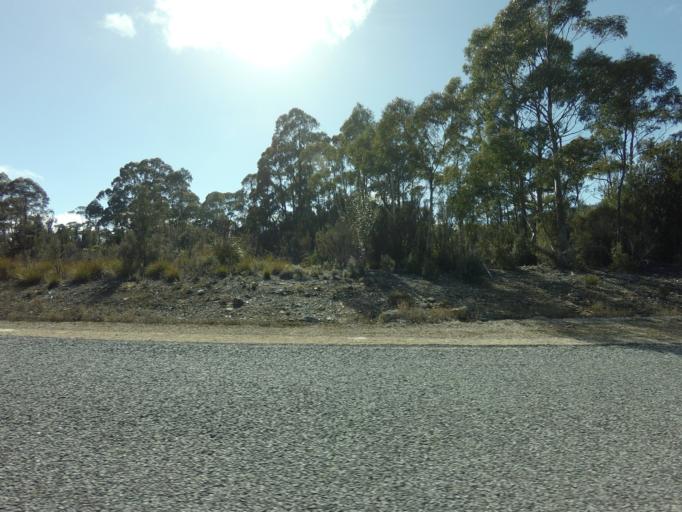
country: AU
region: Tasmania
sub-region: Huon Valley
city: Geeveston
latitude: -42.7726
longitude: 146.3975
